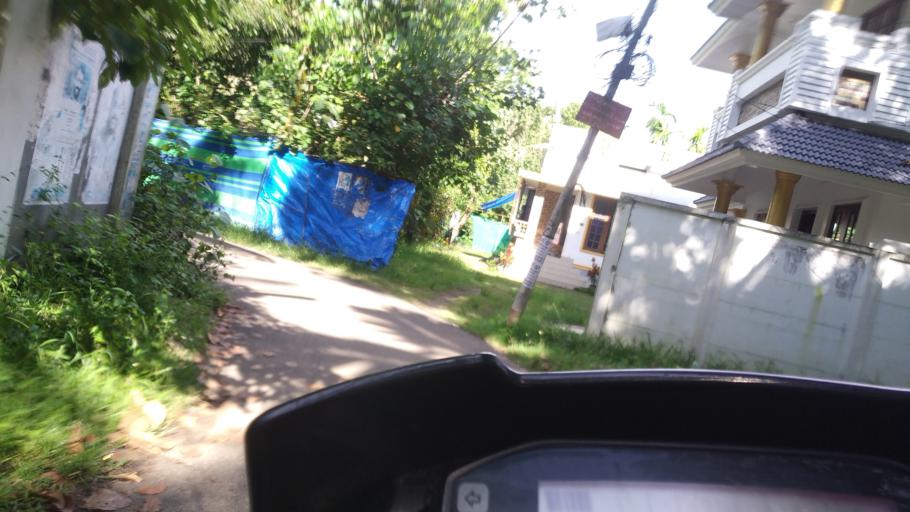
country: IN
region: Kerala
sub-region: Ernakulam
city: Elur
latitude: 10.0729
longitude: 76.2156
